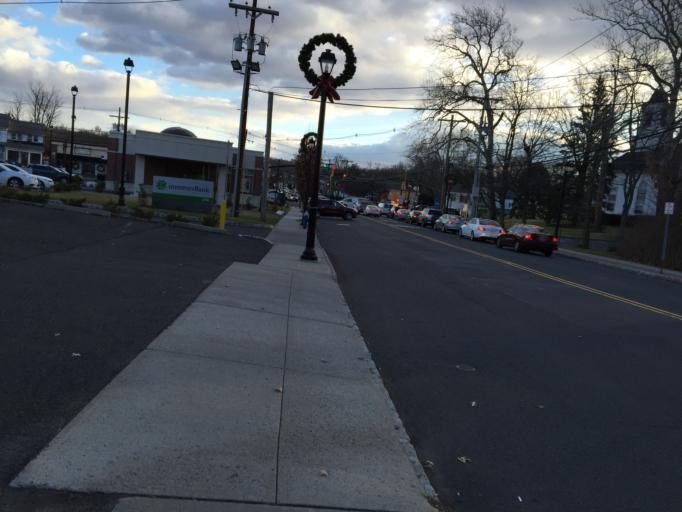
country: US
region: New Jersey
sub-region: Union County
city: New Providence
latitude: 40.7069
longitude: -74.4065
